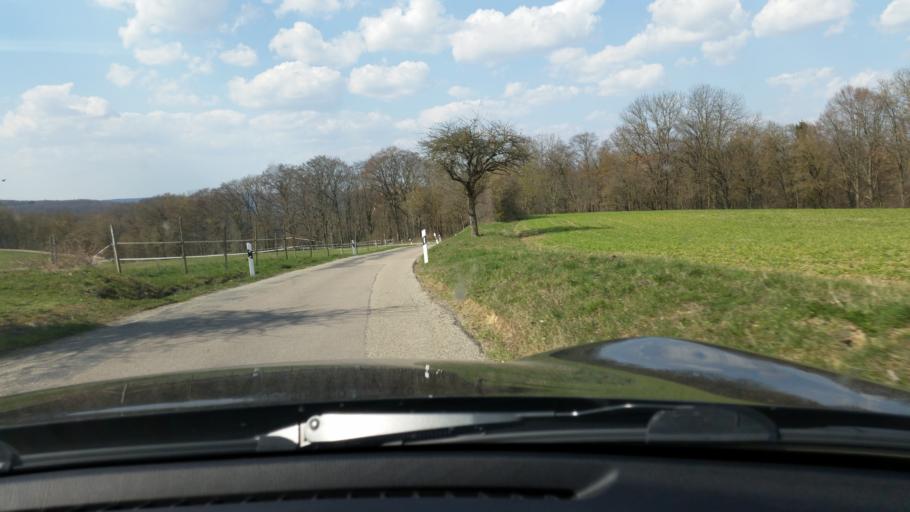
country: DE
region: Baden-Wuerttemberg
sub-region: Regierungsbezirk Stuttgart
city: Braunsbach
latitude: 49.2638
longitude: 9.7819
